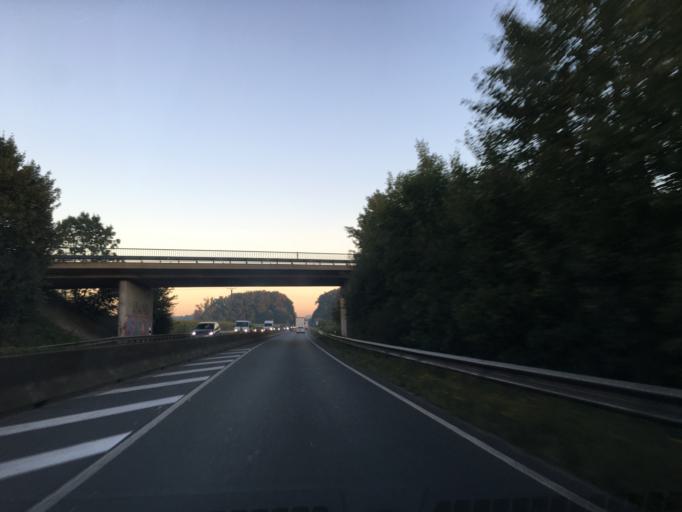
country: DE
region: North Rhine-Westphalia
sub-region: Regierungsbezirk Munster
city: Altenberge
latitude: 52.0137
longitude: 7.5012
